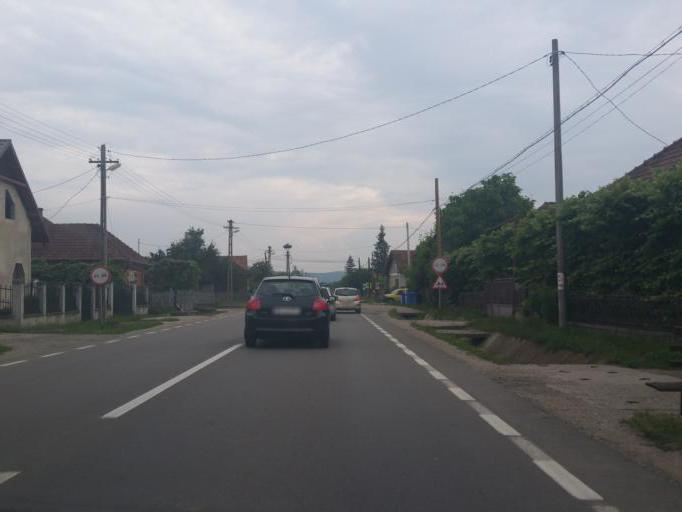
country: RO
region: Salaj
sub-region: Comuna Zimbor
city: Zimbor
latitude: 47.0075
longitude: 23.2604
